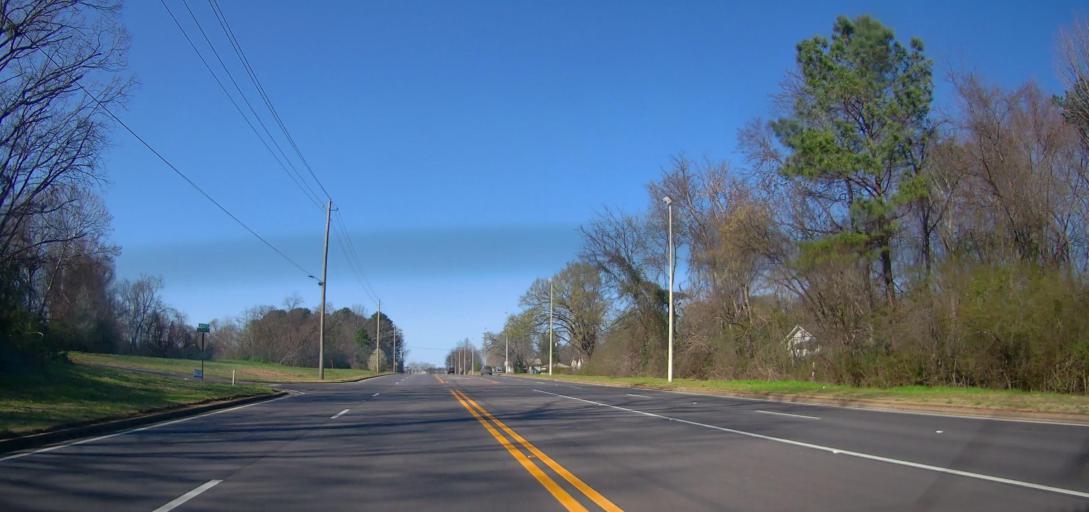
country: US
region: Alabama
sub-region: Lauderdale County
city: East Florence
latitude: 34.8186
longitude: -87.6265
